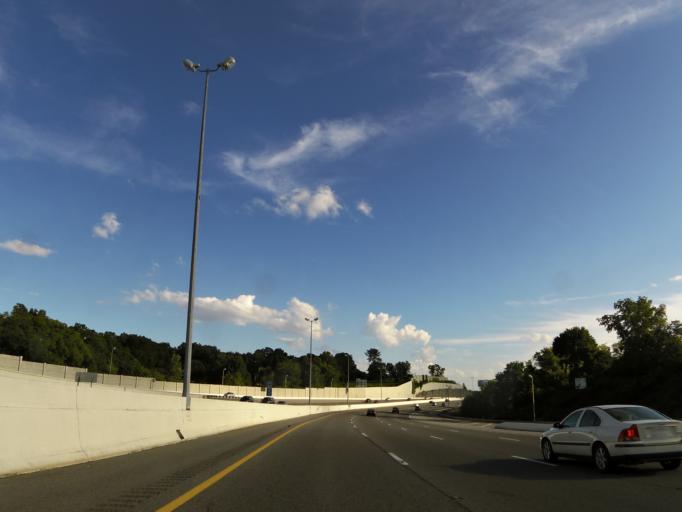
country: US
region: Tennessee
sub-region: Davidson County
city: Lakewood
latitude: 36.1672
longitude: -86.6884
